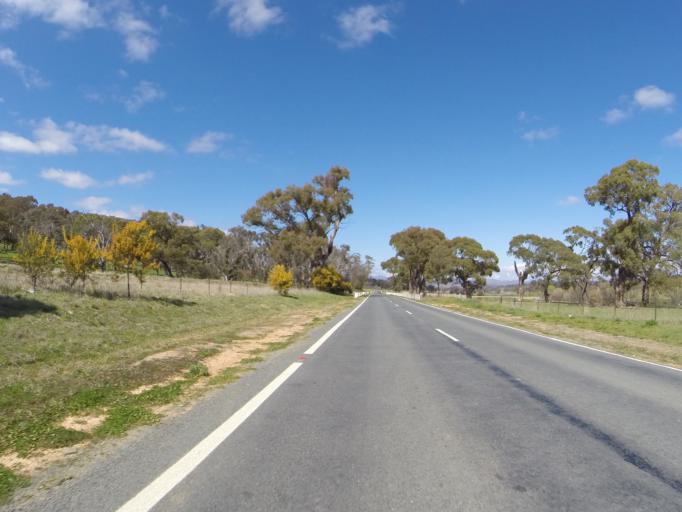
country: AU
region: New South Wales
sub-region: Queanbeyan
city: Queanbeyan
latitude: -35.3024
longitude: 149.2518
